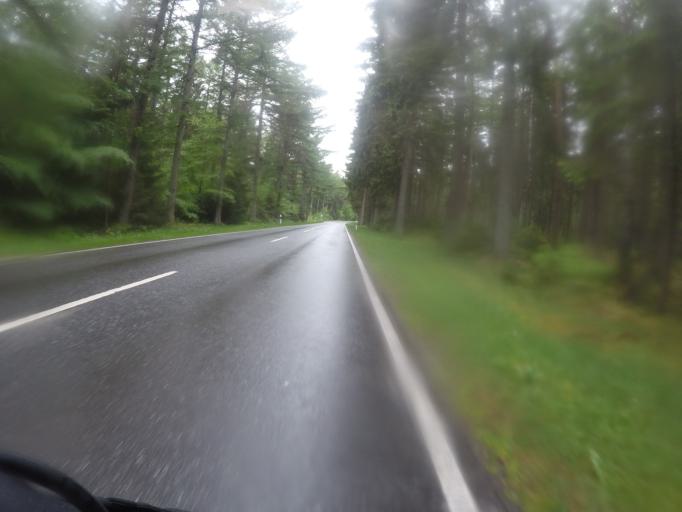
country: DE
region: Schleswig-Holstein
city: Hartenholm
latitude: 53.9304
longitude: 10.0882
